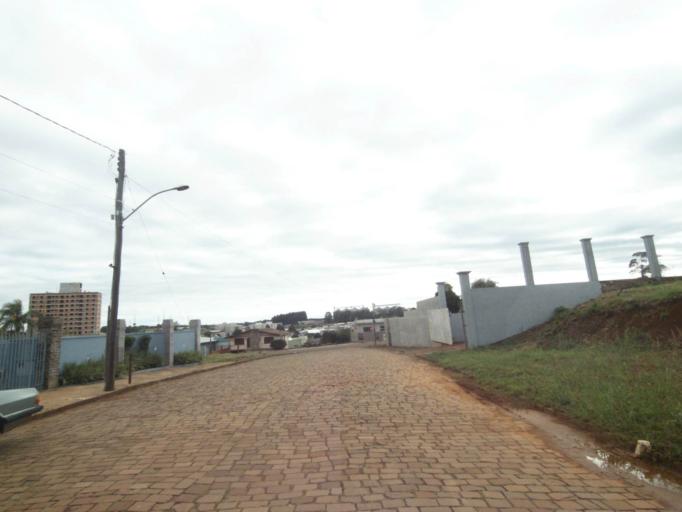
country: BR
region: Rio Grande do Sul
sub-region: Lagoa Vermelha
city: Lagoa Vermelha
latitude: -28.2154
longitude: -51.5157
